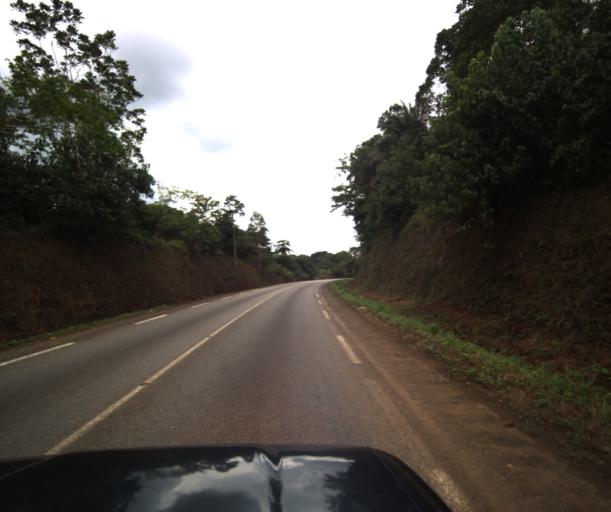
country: CM
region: Littoral
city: Edea
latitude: 3.8368
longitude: 10.4614
